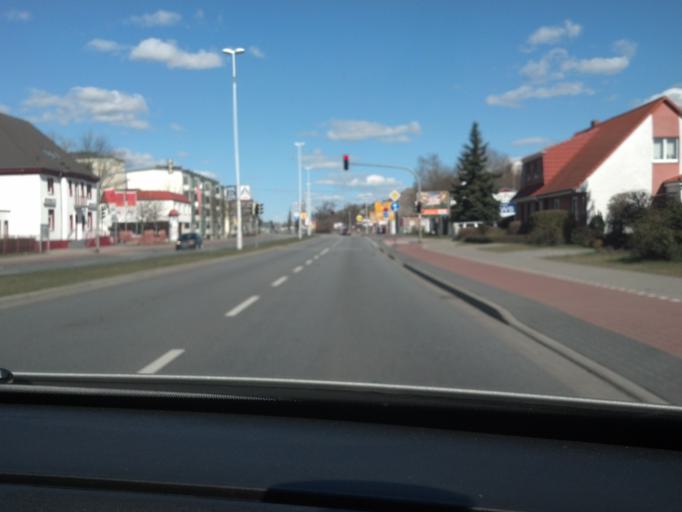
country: DE
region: Mecklenburg-Vorpommern
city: Neubrandenburg
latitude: 53.5663
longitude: 13.2696
